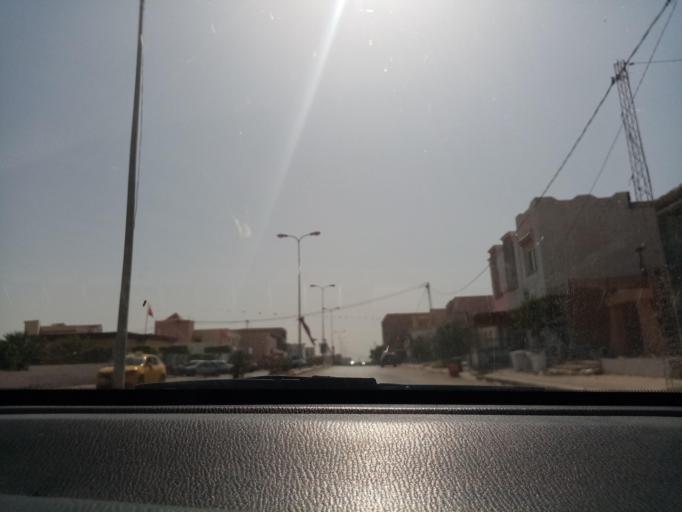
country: TN
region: Qabis
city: Gabes
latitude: 33.8487
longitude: 10.1122
